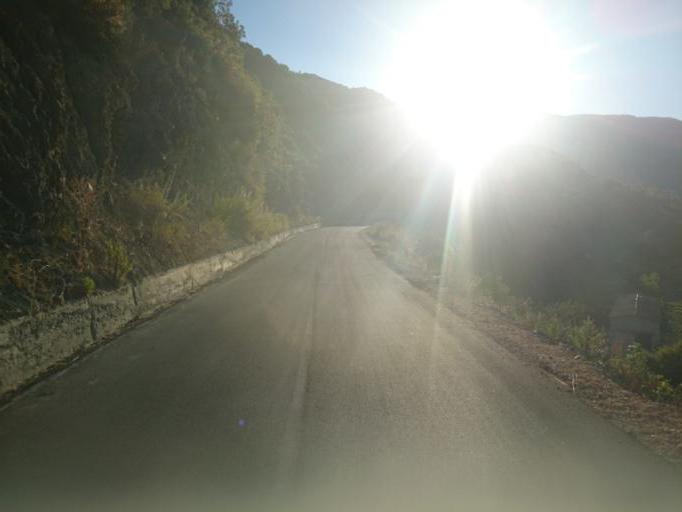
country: AL
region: Berat
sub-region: Rrethi i Skraparit
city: Corovode
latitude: 40.5069
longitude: 20.2102
